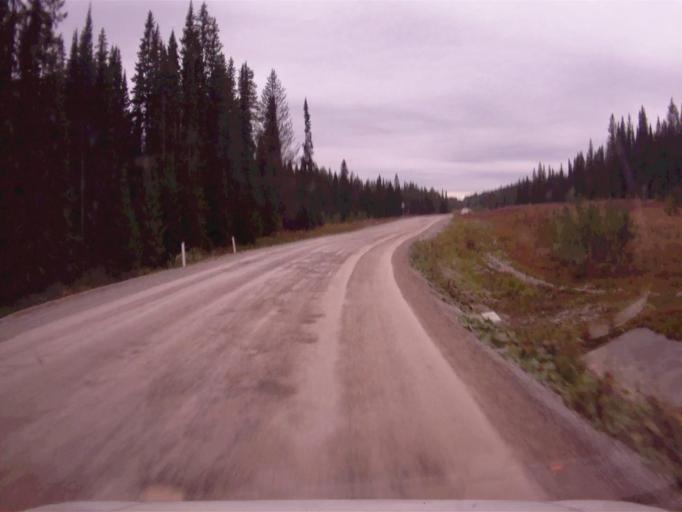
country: RU
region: Chelyabinsk
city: Nyazepetrovsk
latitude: 56.0560
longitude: 59.5515
